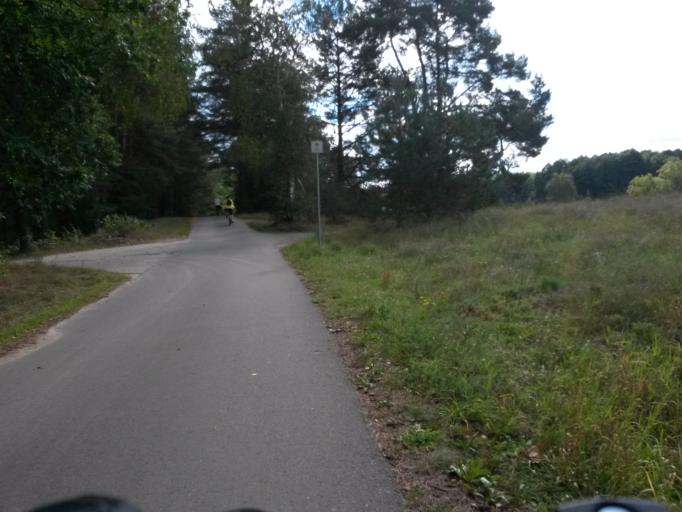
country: DE
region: Brandenburg
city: Milmersdorf
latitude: 53.0749
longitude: 13.5848
